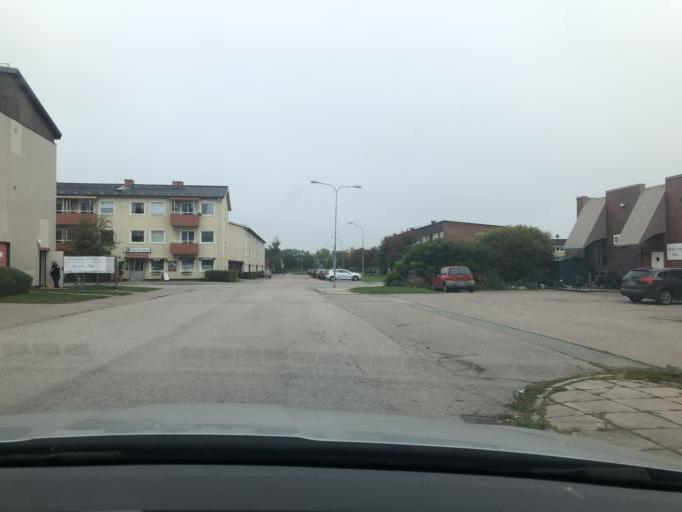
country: SE
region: Uppsala
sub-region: Osthammars Kommun
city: Gimo
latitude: 60.1727
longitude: 18.1840
